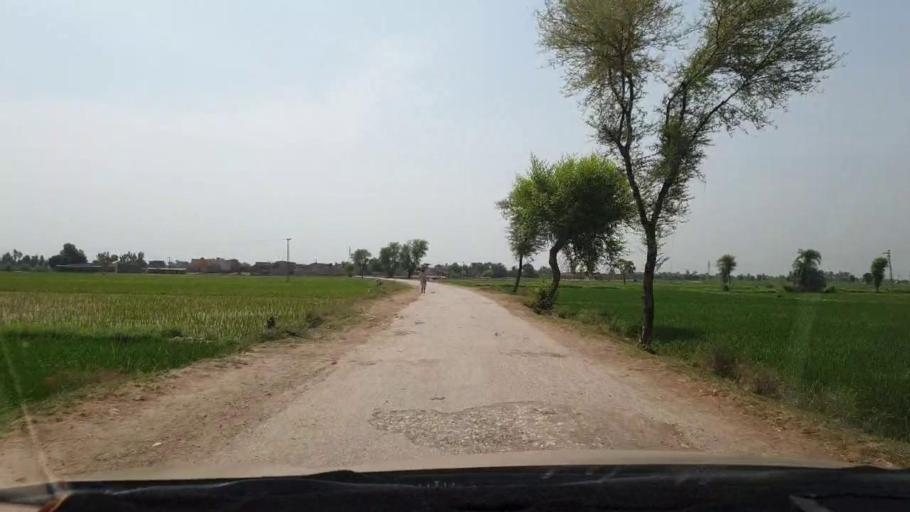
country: PK
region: Sindh
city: Naudero
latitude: 27.6362
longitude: 68.2734
